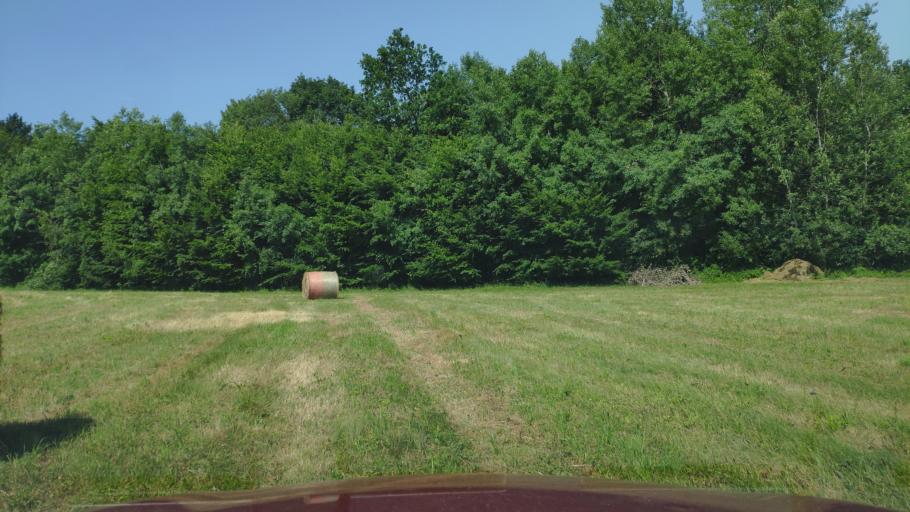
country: SK
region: Presovsky
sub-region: Okres Presov
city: Presov
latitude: 48.9419
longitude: 21.1681
